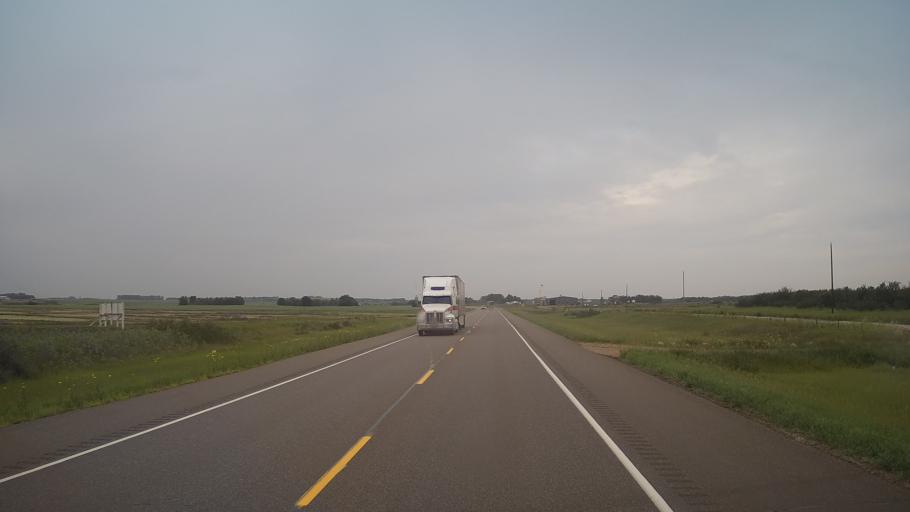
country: CA
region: Saskatchewan
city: Dalmeny
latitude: 52.1293
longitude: -106.8901
